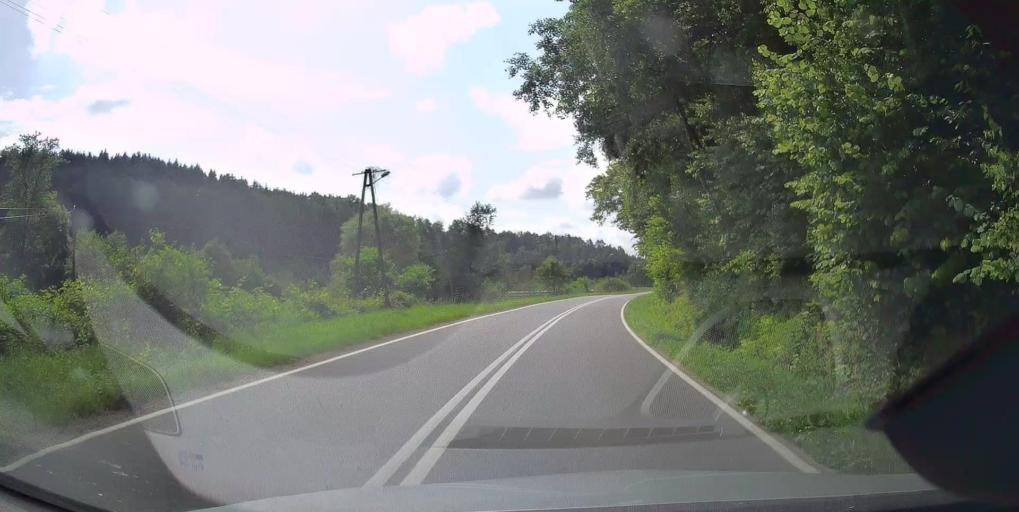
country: PL
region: Lesser Poland Voivodeship
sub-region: Powiat tarnowski
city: Zakliczyn
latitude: 49.8049
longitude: 20.7978
